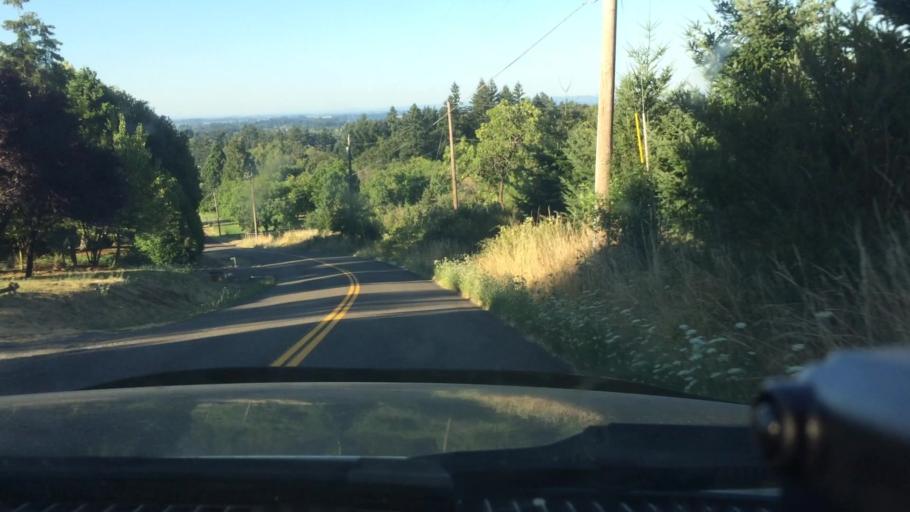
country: US
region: Oregon
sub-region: Yamhill County
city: Newberg
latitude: 45.3283
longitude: -122.9402
